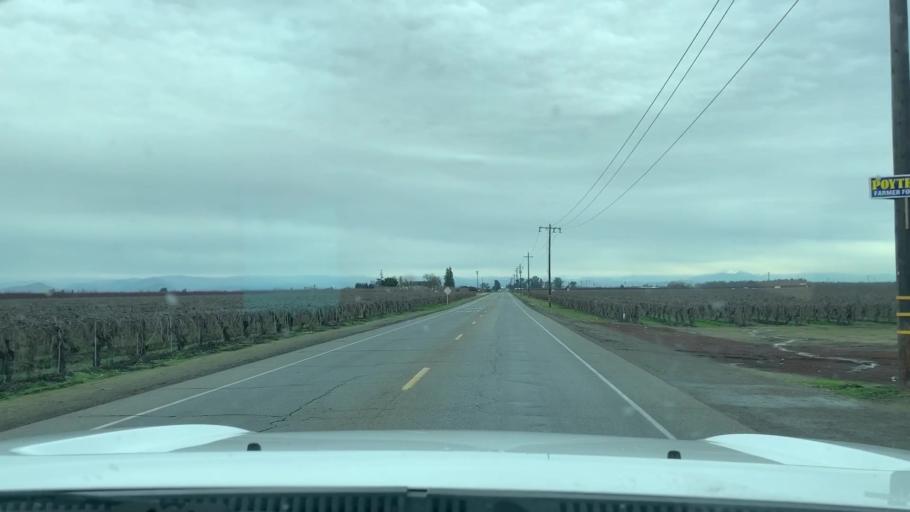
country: US
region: California
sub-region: Fresno County
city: Fowler
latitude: 36.6055
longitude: -119.6813
